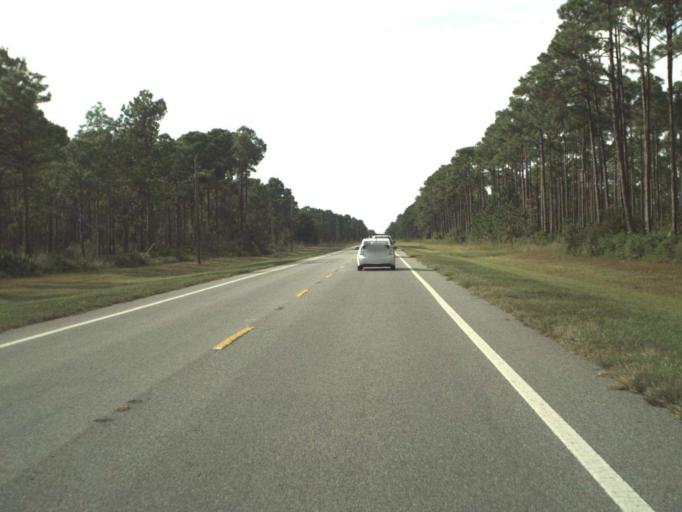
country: US
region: Florida
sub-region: Bay County
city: Tyndall Air Force Base
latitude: 30.0329
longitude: -85.5421
